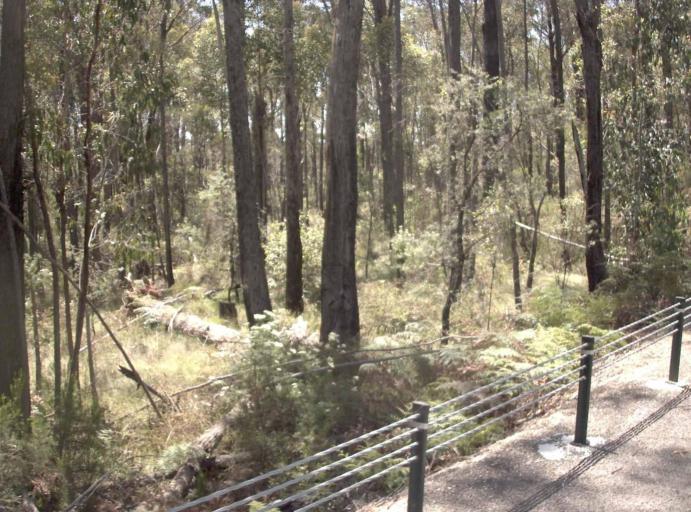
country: AU
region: Victoria
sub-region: East Gippsland
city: Lakes Entrance
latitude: -37.6957
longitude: 148.5900
